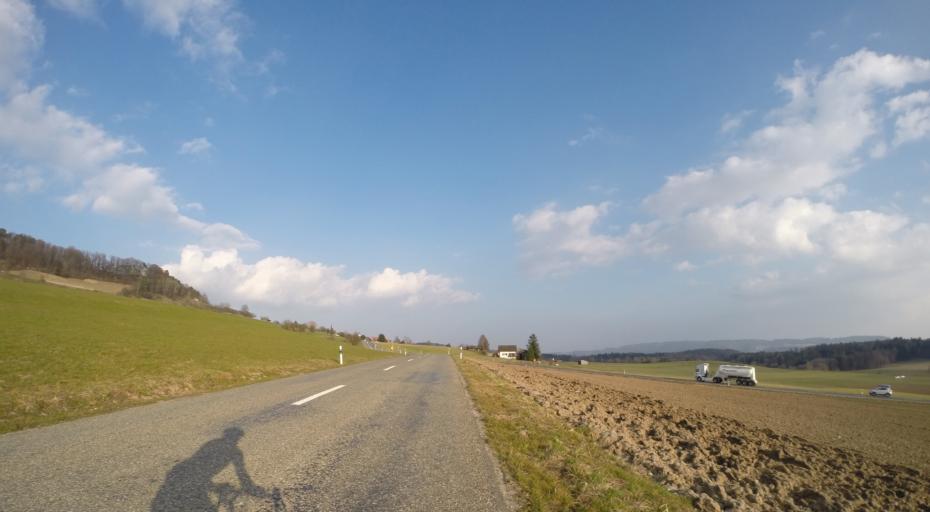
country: CH
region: Thurgau
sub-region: Frauenfeld District
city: Huttwilen
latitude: 47.6029
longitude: 8.8961
